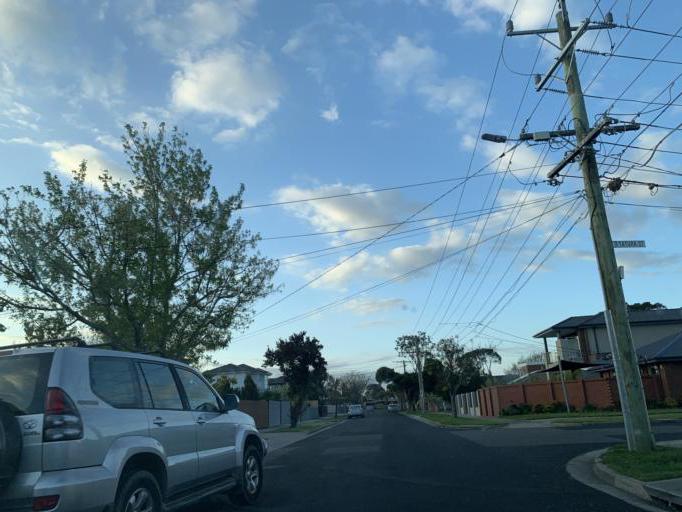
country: AU
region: Victoria
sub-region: Kingston
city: Mentone
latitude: -37.9734
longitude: 145.0805
